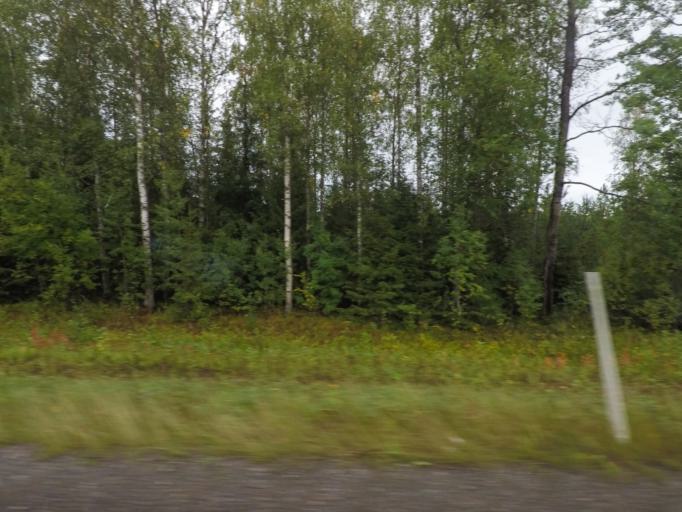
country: FI
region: Southern Savonia
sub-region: Pieksaemaeki
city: Joroinen
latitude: 62.1053
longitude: 27.8340
